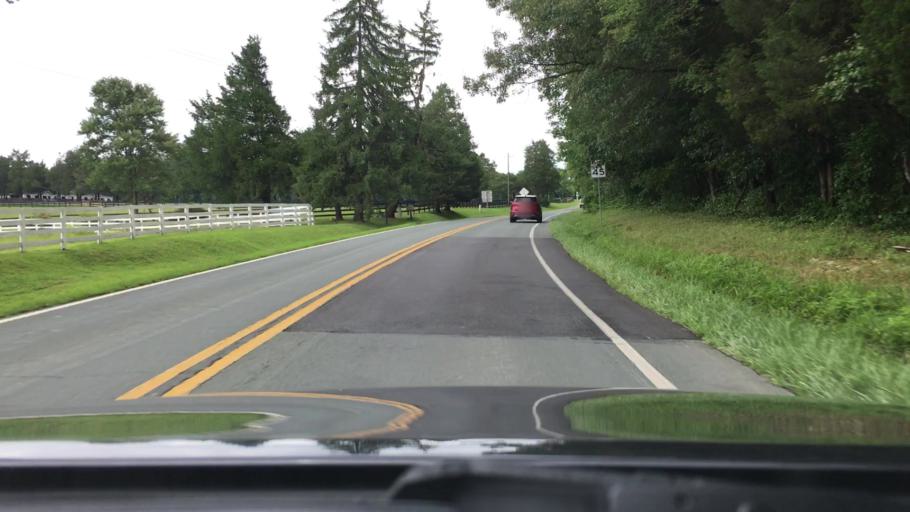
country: US
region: Virginia
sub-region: Fluvanna County
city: Lake Monticello
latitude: 38.0552
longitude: -78.3175
